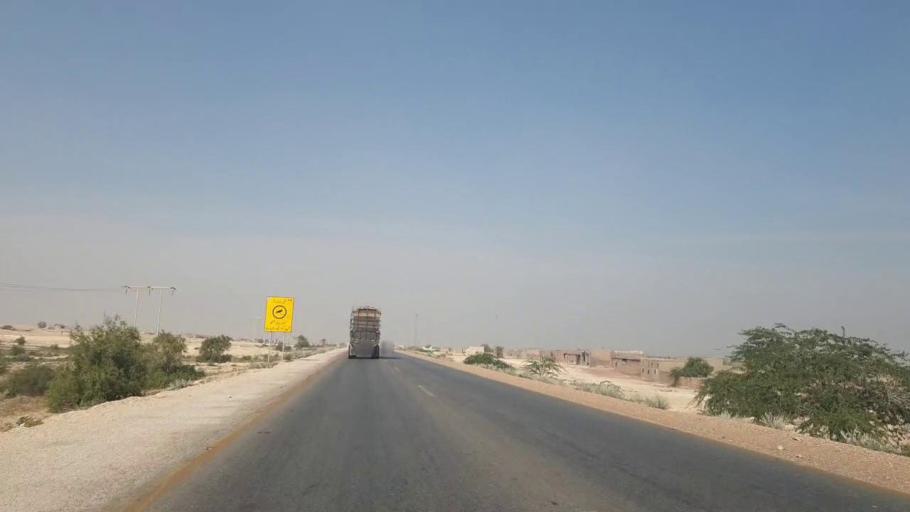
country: PK
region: Sindh
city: Hala
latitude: 25.7777
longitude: 68.2844
